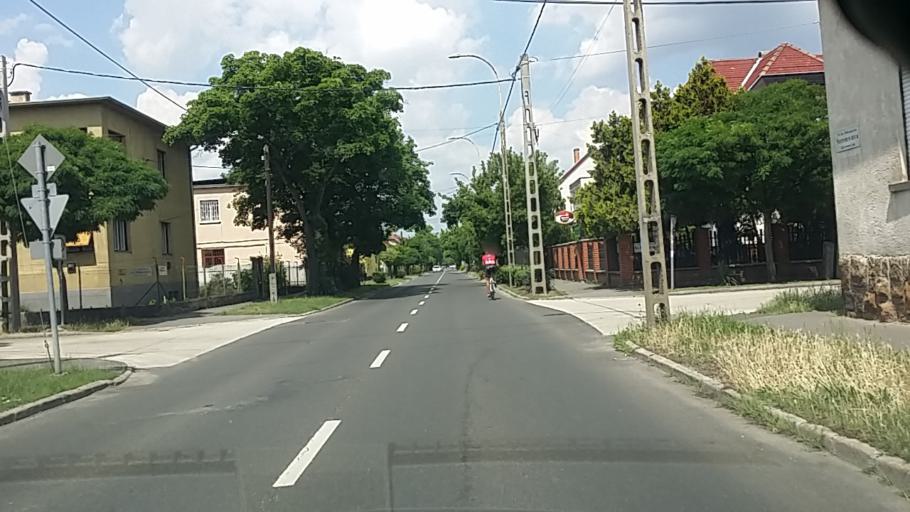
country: HU
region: Budapest
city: Budapest XV. keruelet
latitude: 47.5470
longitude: 19.1262
